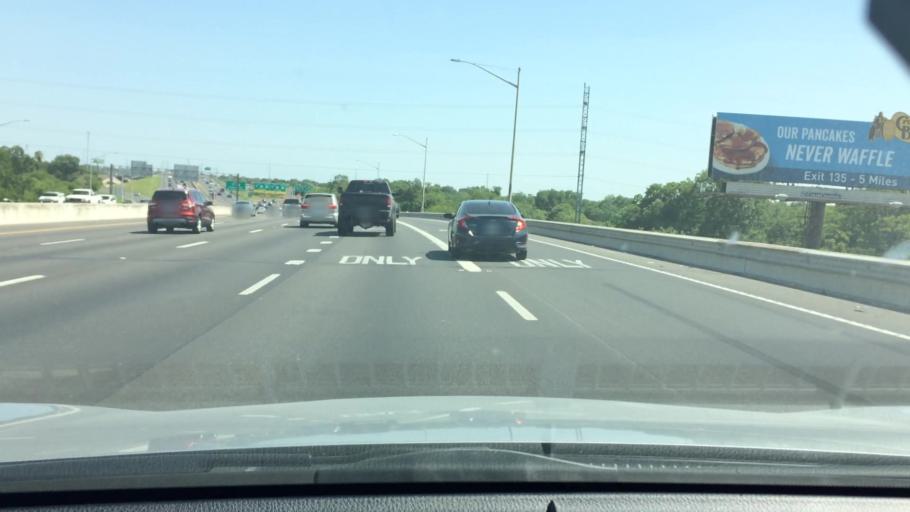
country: US
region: Texas
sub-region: Bexar County
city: San Antonio
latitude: 29.4020
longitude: -98.4812
